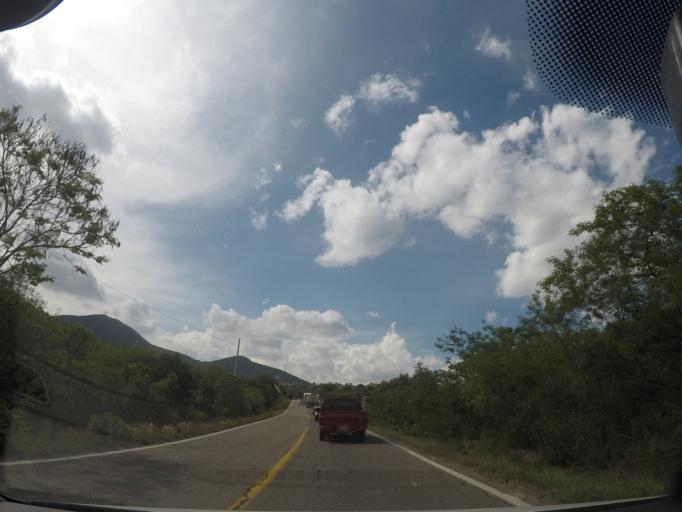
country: MX
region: Oaxaca
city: San Dionisio Ocotepec
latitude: 16.8008
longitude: -96.3526
